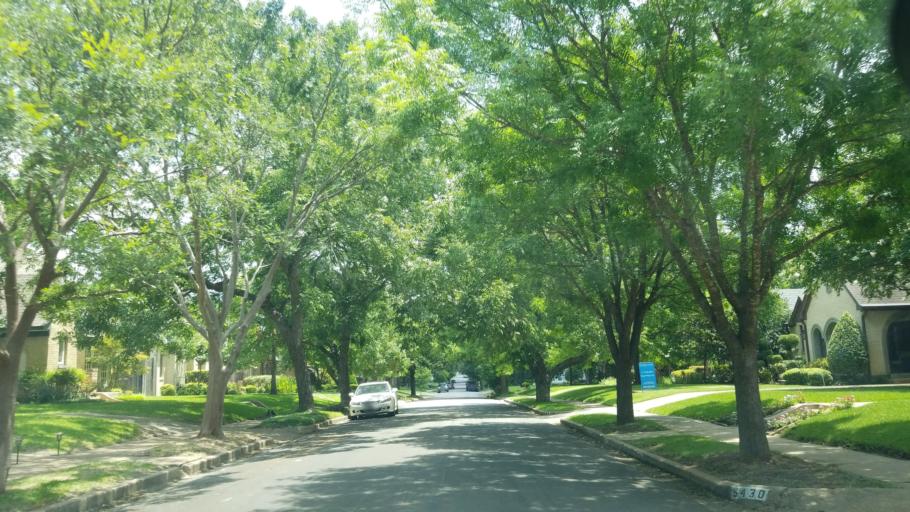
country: US
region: Texas
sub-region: Dallas County
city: Highland Park
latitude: 32.8273
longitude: -96.7761
